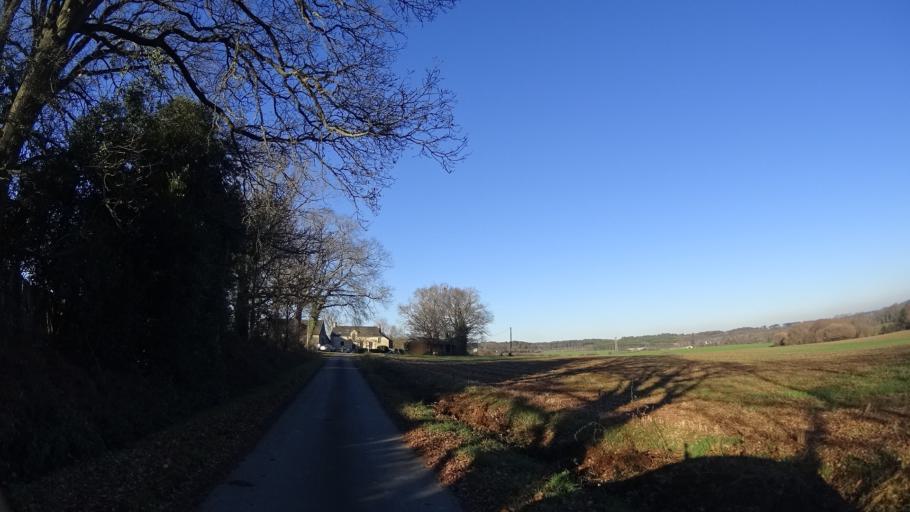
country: FR
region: Brittany
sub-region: Departement du Morbihan
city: Allaire
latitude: 47.6692
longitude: -2.1812
